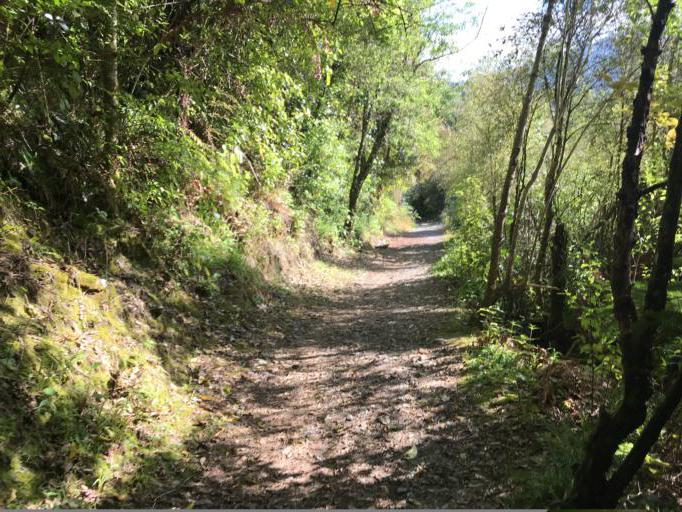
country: NZ
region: Wellington
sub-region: Kapiti Coast District
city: Otaki
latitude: -40.8718
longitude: 175.2321
